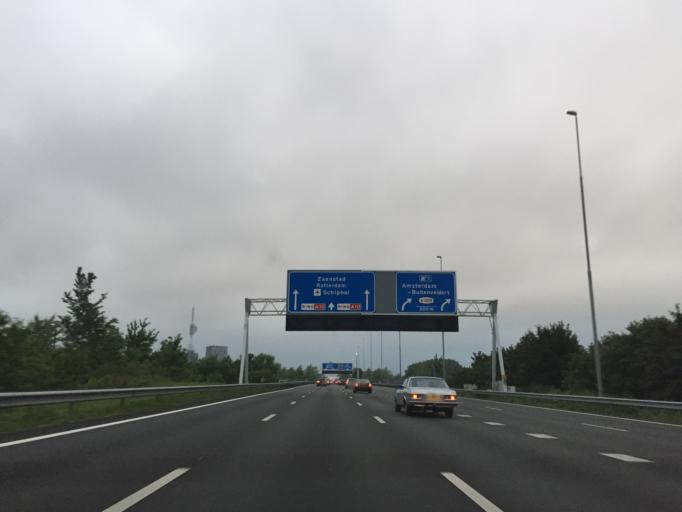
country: NL
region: North Holland
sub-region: Gemeente Ouder-Amstel
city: Ouderkerk aan de Amstel
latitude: 52.3318
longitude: 4.9015
